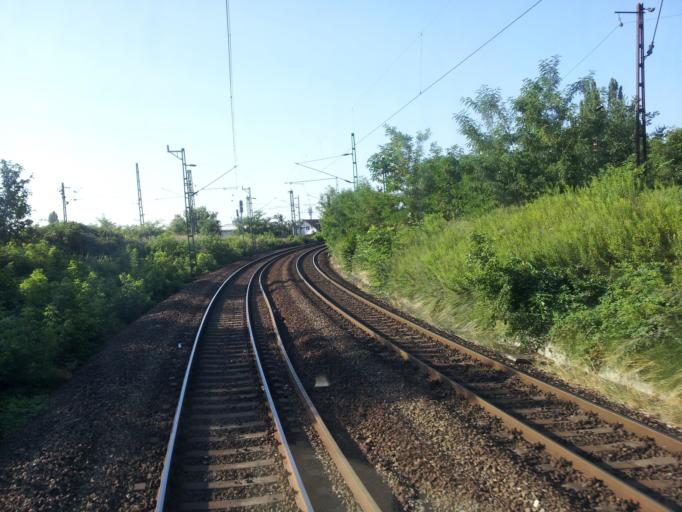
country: HU
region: Budapest
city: Budapest XIV. keruelet
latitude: 47.4868
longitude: 19.1190
